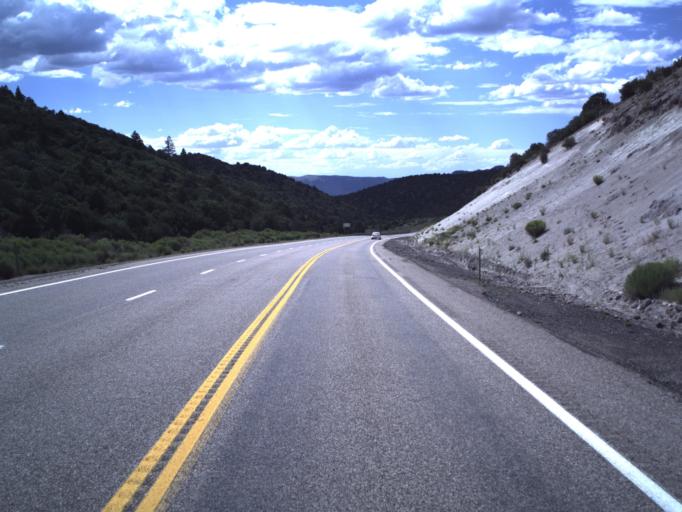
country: US
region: Utah
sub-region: Garfield County
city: Panguitch
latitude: 38.0350
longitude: -112.5405
